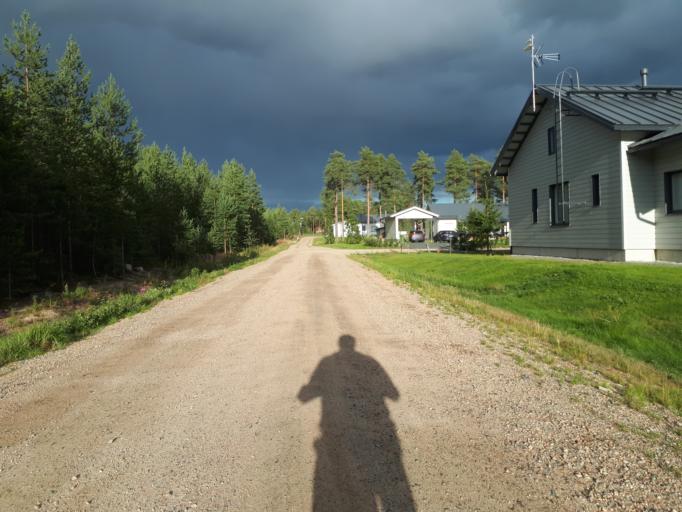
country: FI
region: Northern Ostrobothnia
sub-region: Oulunkaari
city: Ii
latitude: 65.3248
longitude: 25.3993
